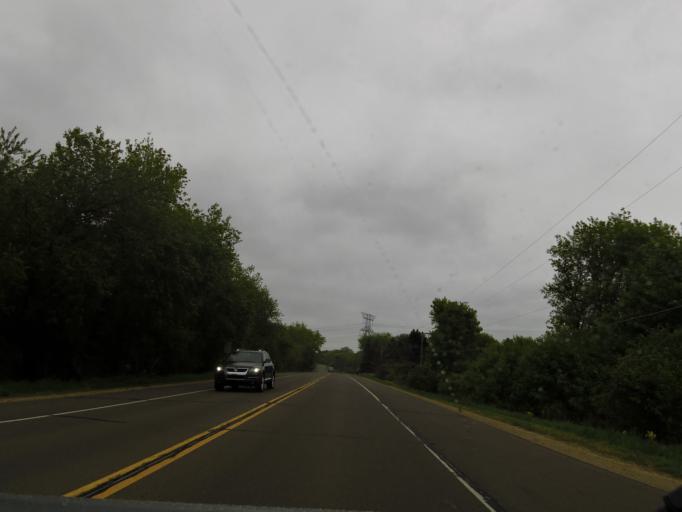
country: US
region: Minnesota
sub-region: Washington County
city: Oak Park Heights
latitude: 45.0077
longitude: -92.8207
